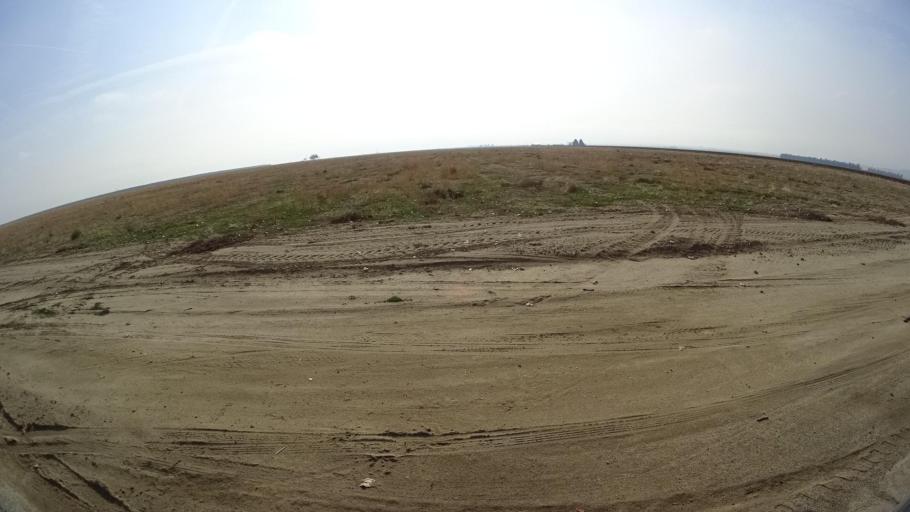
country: US
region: California
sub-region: Kern County
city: Lebec
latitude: 35.0309
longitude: -118.9074
